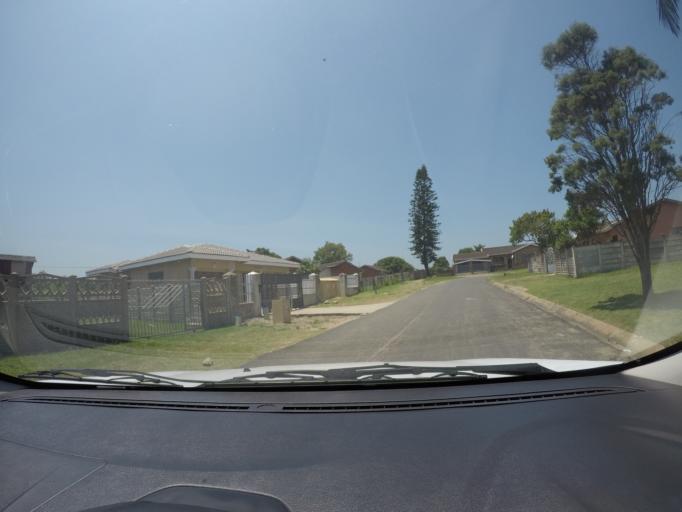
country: ZA
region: KwaZulu-Natal
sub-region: uThungulu District Municipality
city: eSikhawini
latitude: -28.8707
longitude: 31.9091
